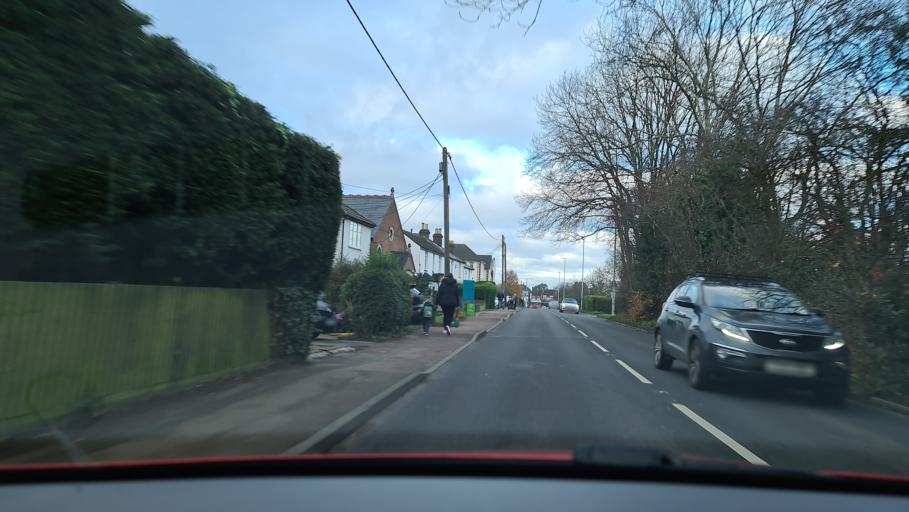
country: GB
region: England
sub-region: Buckinghamshire
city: High Wycombe
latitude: 51.6510
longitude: -0.7083
